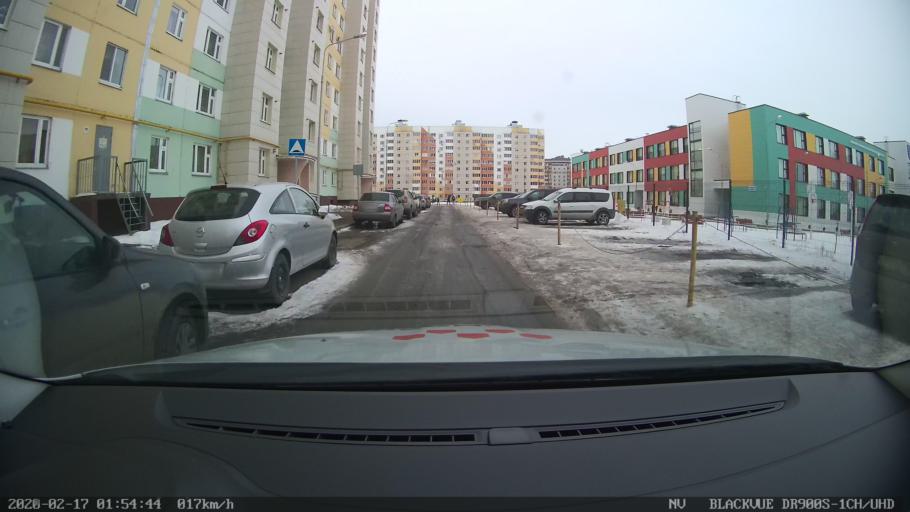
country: RU
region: Tatarstan
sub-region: Gorod Kazan'
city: Kazan
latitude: 55.8038
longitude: 49.2132
